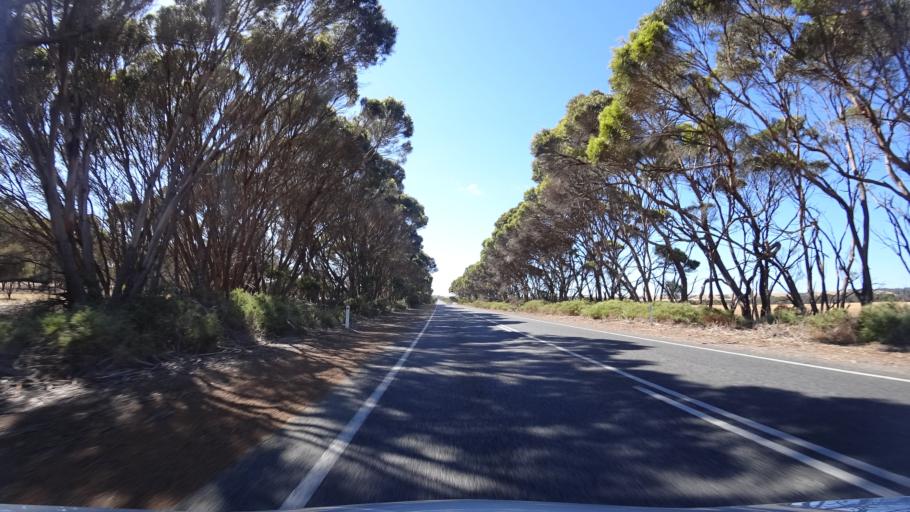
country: AU
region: South Australia
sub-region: Kangaroo Island
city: Kingscote
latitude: -35.7321
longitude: 137.5679
